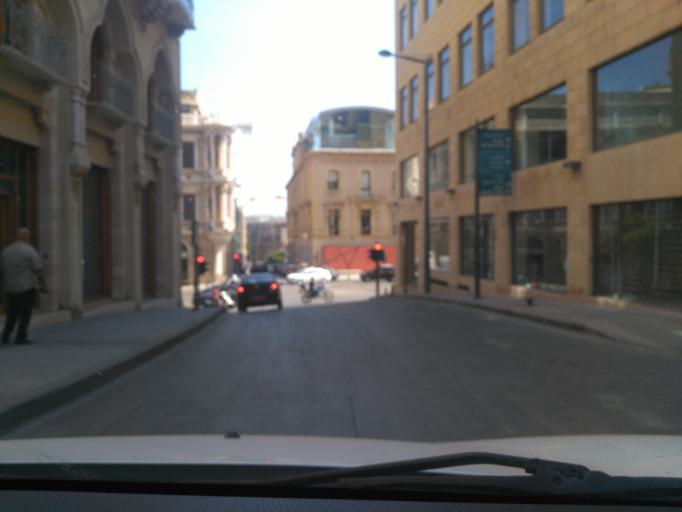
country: LB
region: Beyrouth
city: Beirut
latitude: 33.8983
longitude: 35.5023
